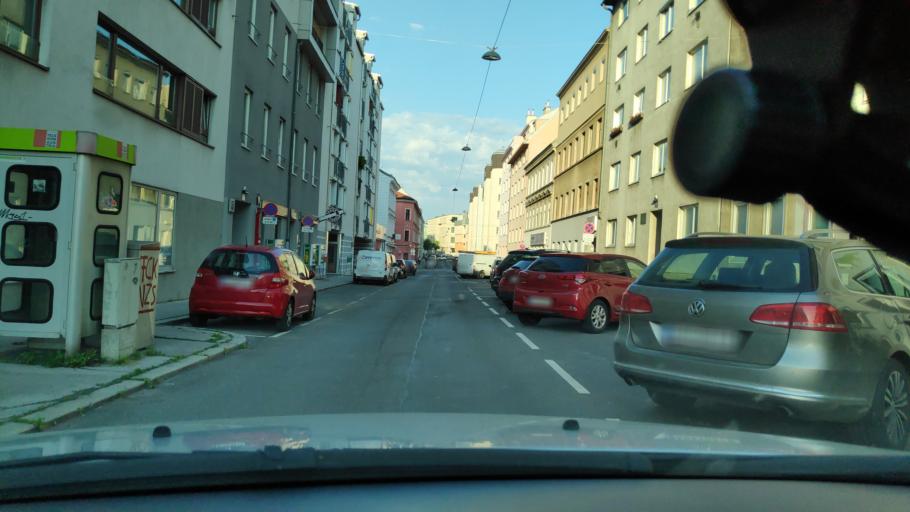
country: AT
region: Vienna
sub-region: Wien Stadt
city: Vienna
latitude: 48.2169
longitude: 16.3243
